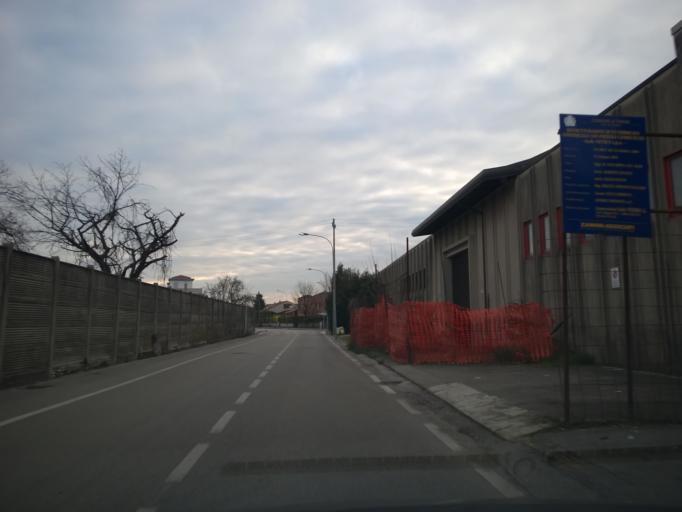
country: IT
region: Veneto
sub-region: Provincia di Vicenza
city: Thiene
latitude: 45.6963
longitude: 11.4846
